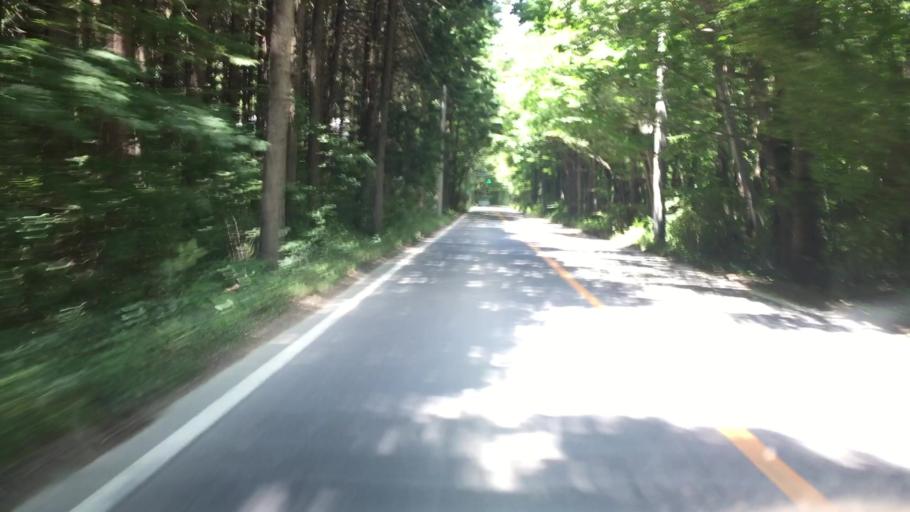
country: JP
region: Tochigi
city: Kuroiso
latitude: 37.0322
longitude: 139.9921
